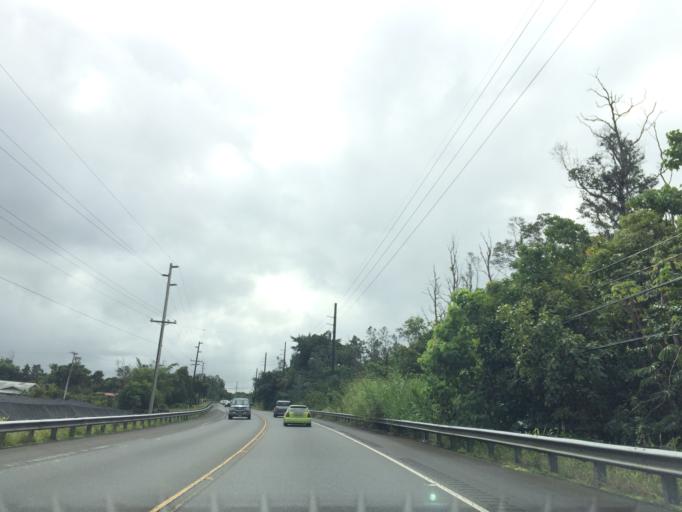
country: US
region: Hawaii
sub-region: Hawaii County
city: Hawaiian Paradise Park
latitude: 19.5124
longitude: -154.9624
